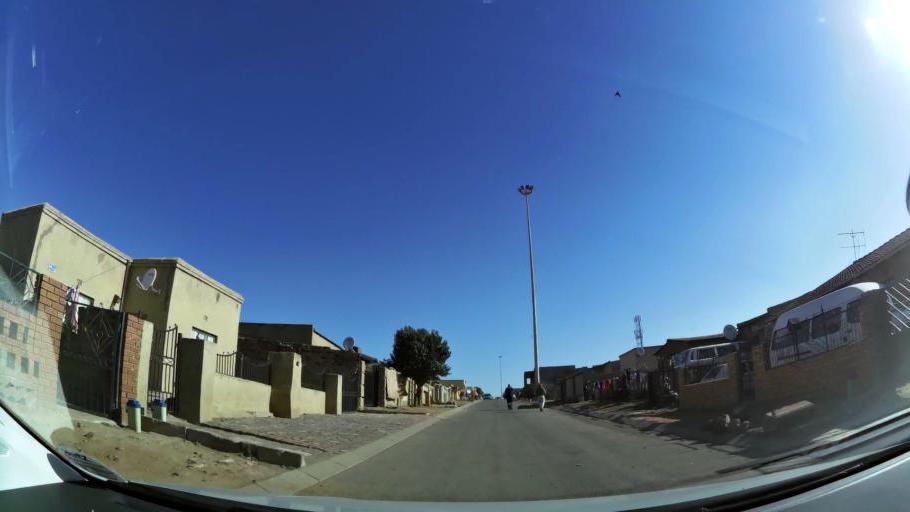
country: ZA
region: Gauteng
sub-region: Ekurhuleni Metropolitan Municipality
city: Tembisa
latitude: -26.0186
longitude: 28.2380
